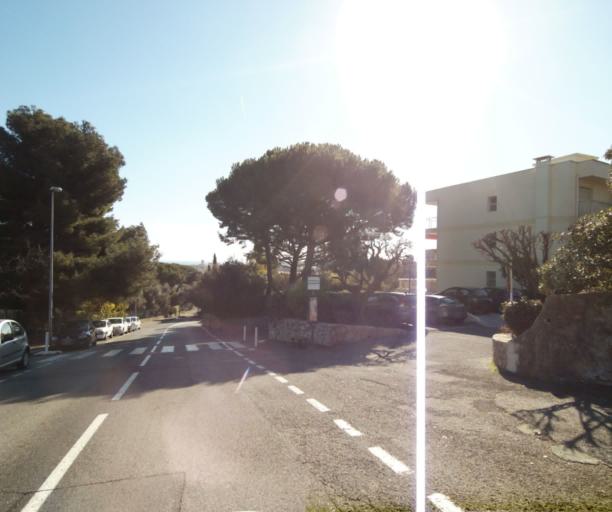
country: FR
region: Provence-Alpes-Cote d'Azur
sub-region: Departement des Alpes-Maritimes
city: Antibes
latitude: 43.5883
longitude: 7.1149
